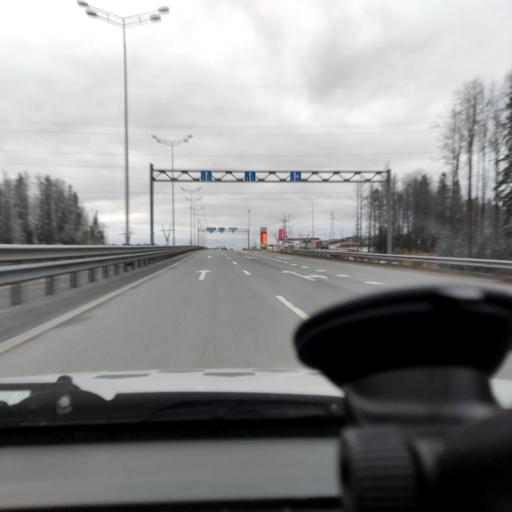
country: RU
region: Perm
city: Novyye Lyady
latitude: 58.0391
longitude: 56.4322
